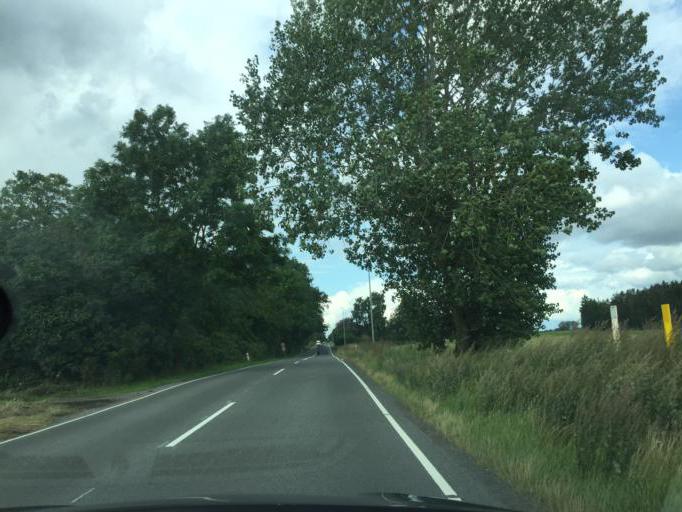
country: DK
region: South Denmark
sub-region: Odense Kommune
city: Stige
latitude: 55.4571
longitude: 10.3637
